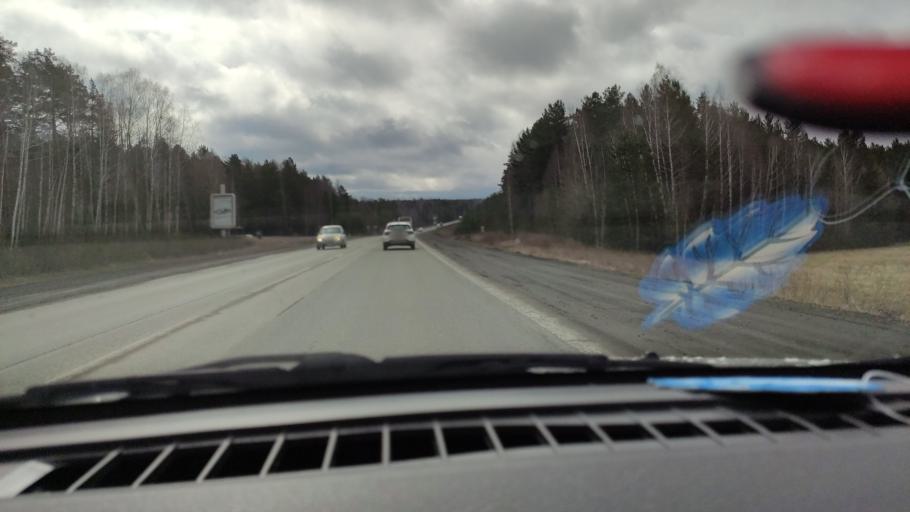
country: RU
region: Sverdlovsk
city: Talitsa
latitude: 56.8658
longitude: 60.0470
